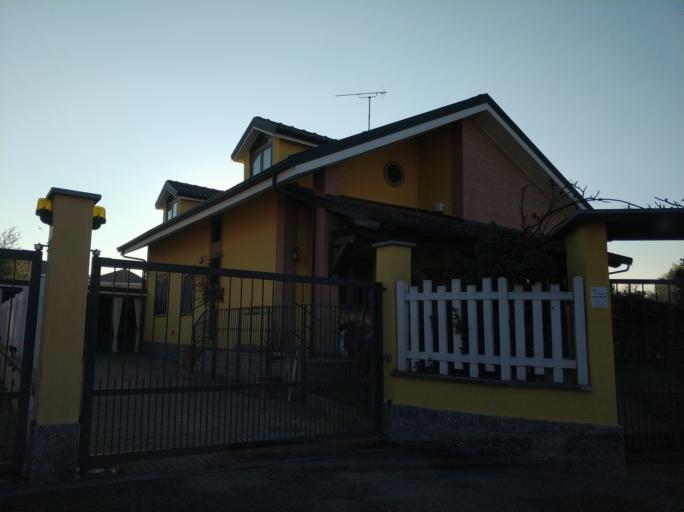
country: IT
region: Piedmont
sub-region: Provincia di Torino
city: San Maurizio
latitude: 45.2150
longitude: 7.6226
